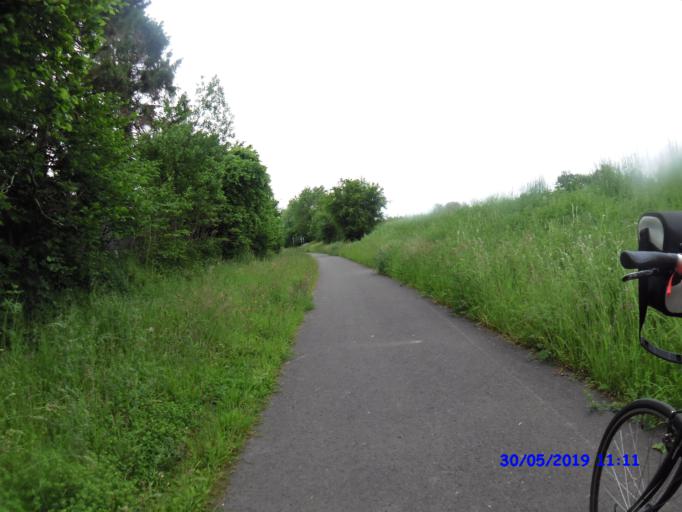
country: BE
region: Wallonia
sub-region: Province du Hainaut
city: Thuin
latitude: 50.2969
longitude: 4.3360
